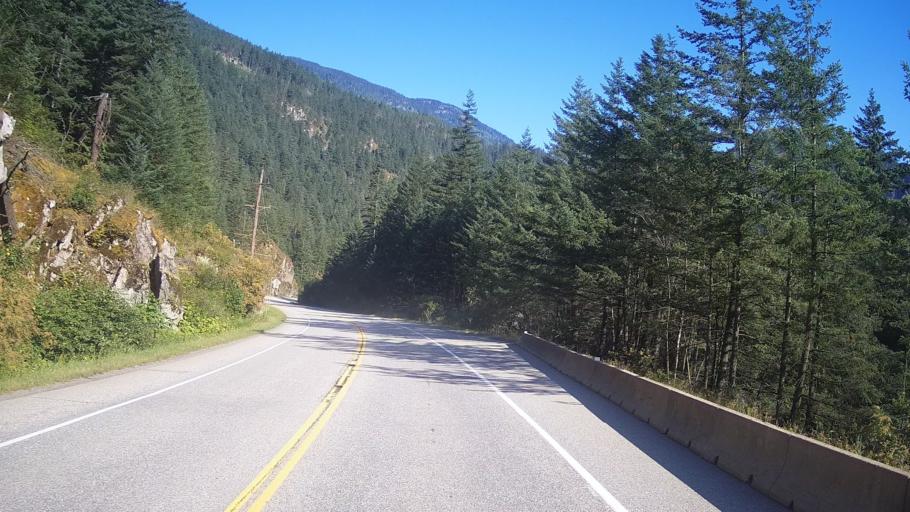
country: CA
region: British Columbia
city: Hope
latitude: 49.5949
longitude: -121.4109
